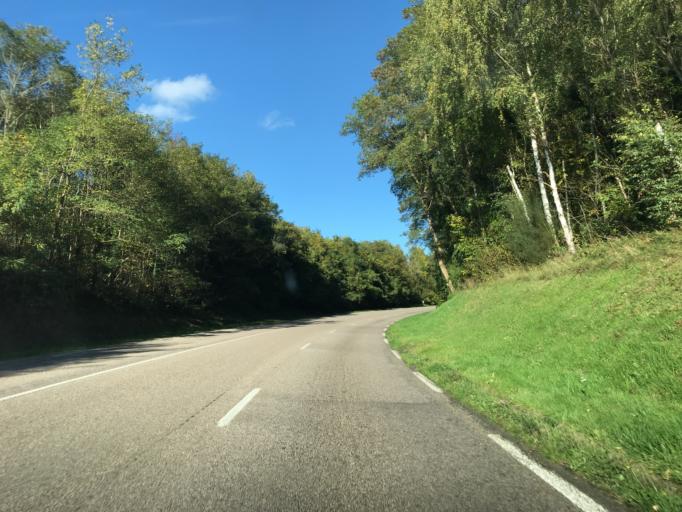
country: FR
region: Haute-Normandie
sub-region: Departement de l'Eure
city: Saint-Aubin-sur-Gaillon
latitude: 49.1108
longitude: 1.2979
